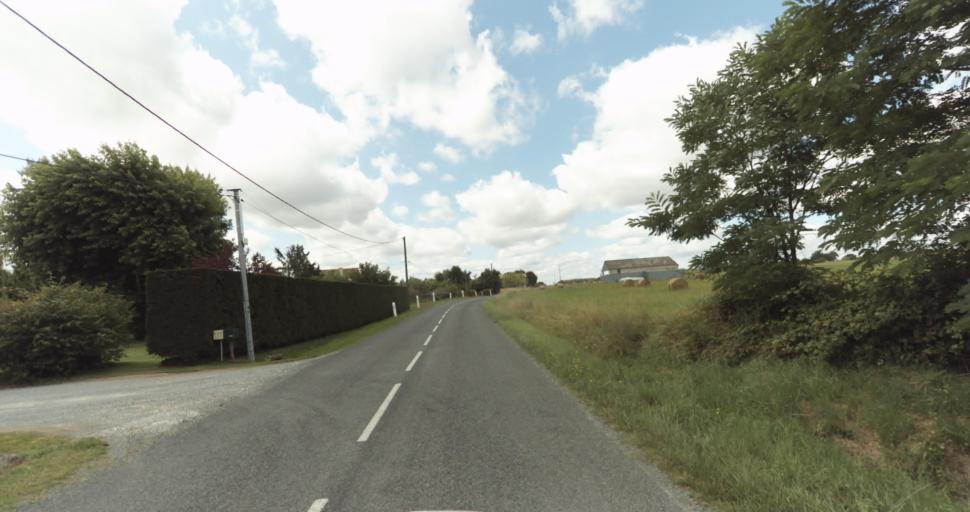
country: FR
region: Aquitaine
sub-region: Departement de la Gironde
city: Bazas
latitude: 44.4645
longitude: -0.1829
